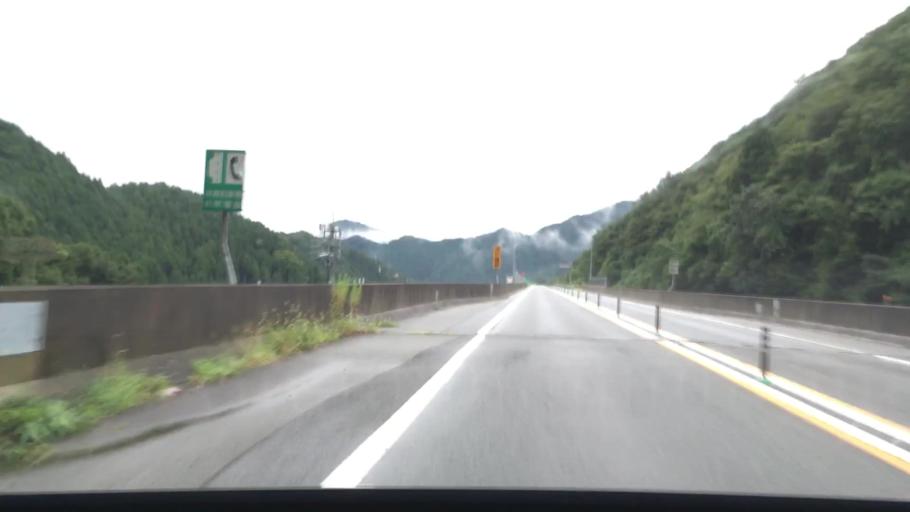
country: JP
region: Hyogo
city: Toyooka
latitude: 35.2508
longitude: 134.7920
